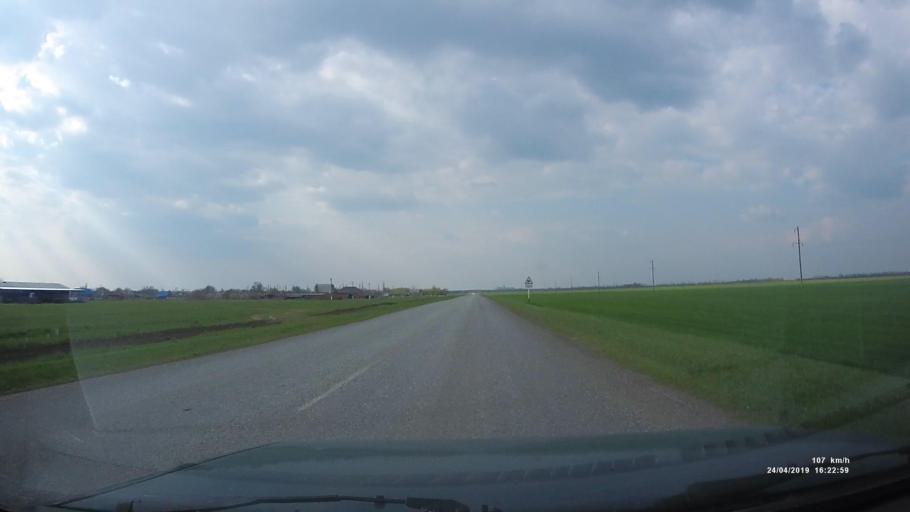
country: RU
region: Rostov
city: Orlovskiy
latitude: 46.8278
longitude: 42.0522
